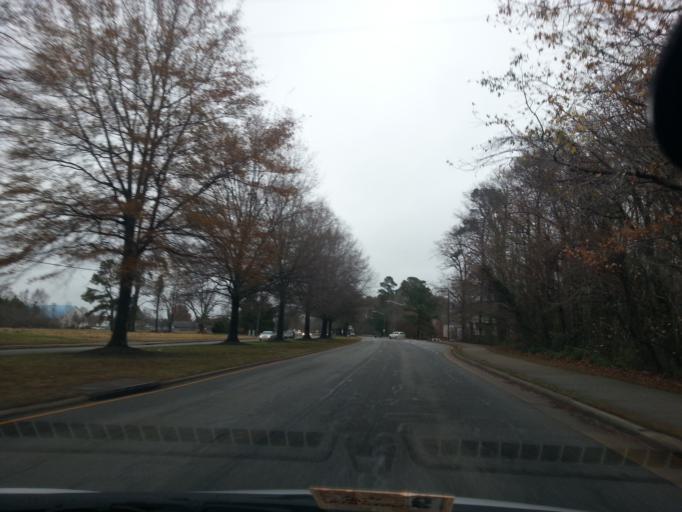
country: US
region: Virginia
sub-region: City of Virginia Beach
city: Virginia Beach
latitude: 36.7760
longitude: -76.0052
